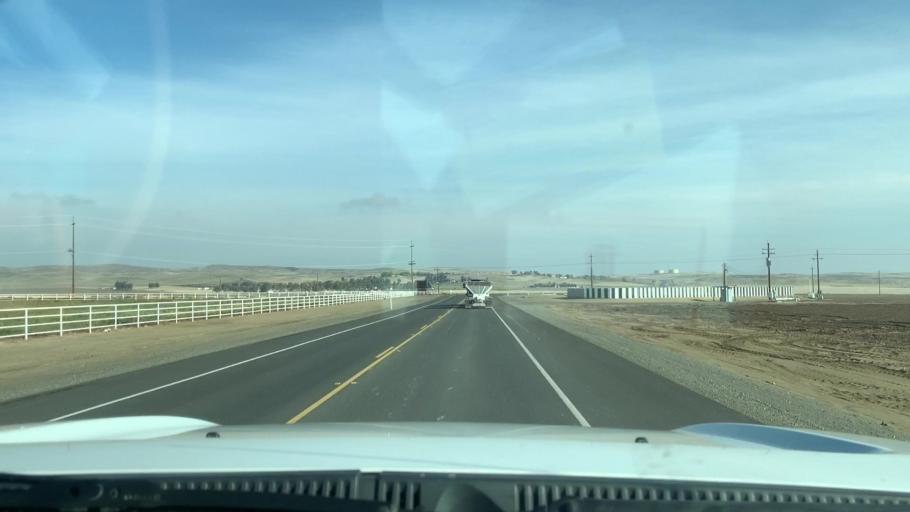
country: US
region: California
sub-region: Fresno County
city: Coalinga
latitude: 36.1926
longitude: -120.3392
